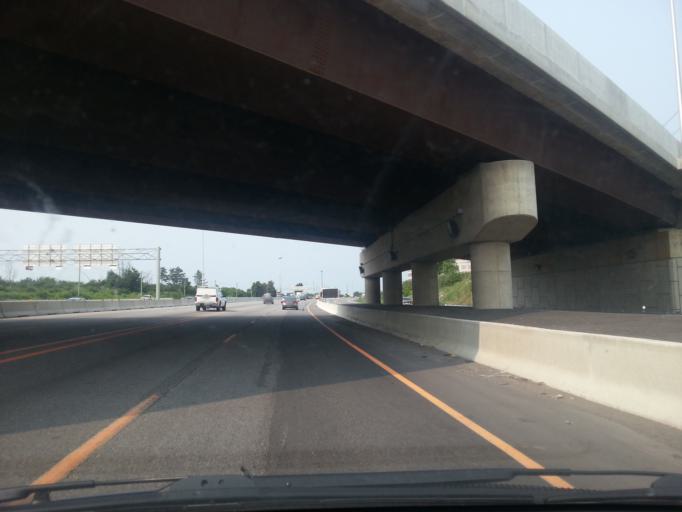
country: CA
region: Ontario
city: Ottawa
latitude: 45.4223
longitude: -75.6249
